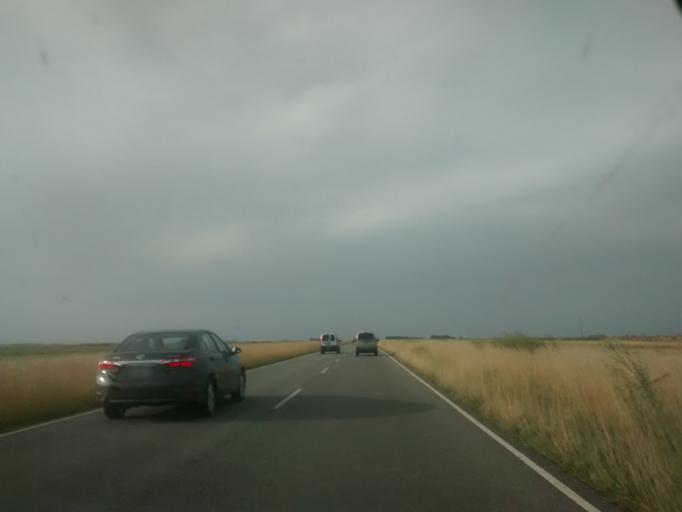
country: AR
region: Buenos Aires
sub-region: Partido de Rauch
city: Rauch
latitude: -36.5100
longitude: -58.5702
